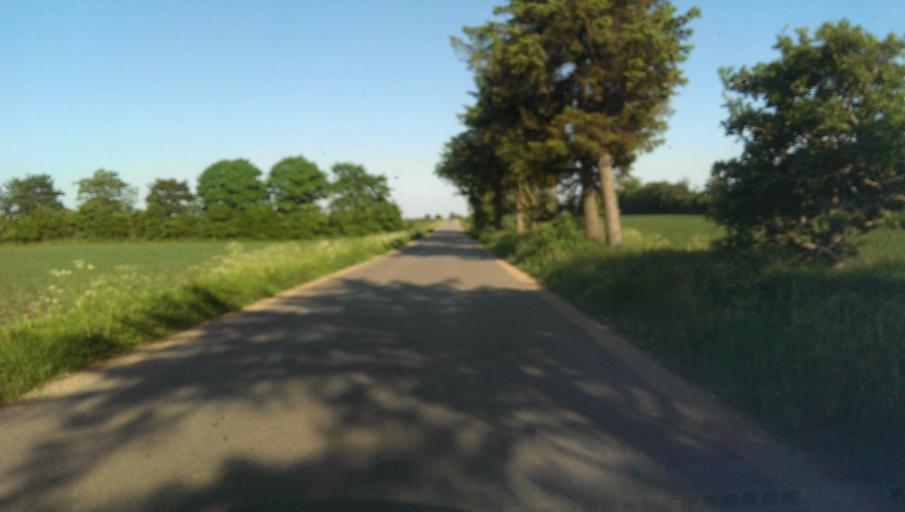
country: DK
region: South Denmark
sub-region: Esbjerg Kommune
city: Bramming
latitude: 55.5502
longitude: 8.6413
